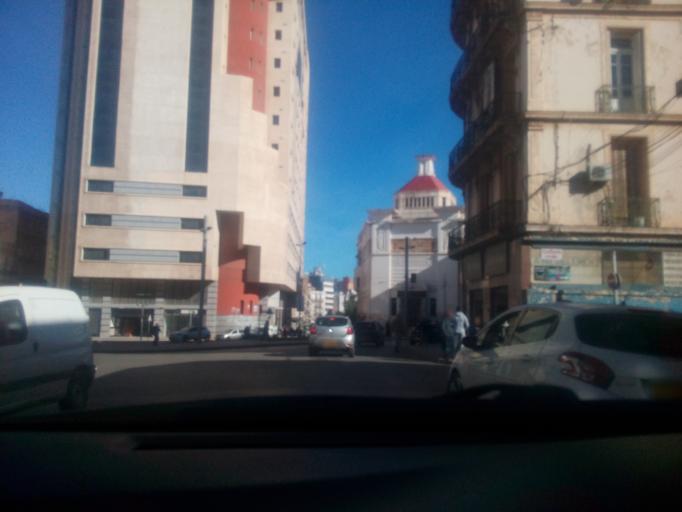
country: DZ
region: Oran
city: Oran
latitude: 35.6998
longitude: -0.6488
